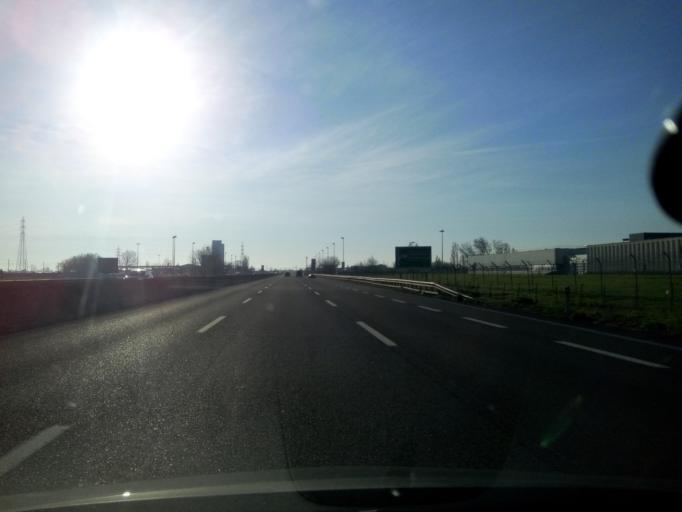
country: IT
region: Emilia-Romagna
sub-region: Provincia di Parma
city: Parma
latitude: 44.8289
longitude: 10.3728
